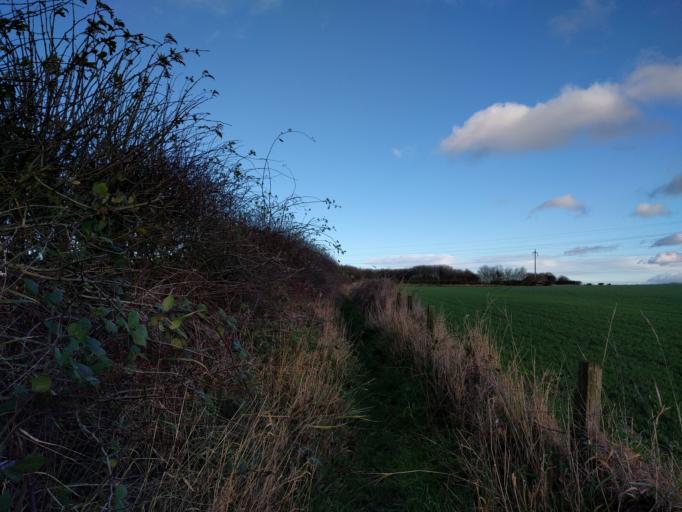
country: GB
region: England
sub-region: Northumberland
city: Bedlington
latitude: 55.1195
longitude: -1.5783
